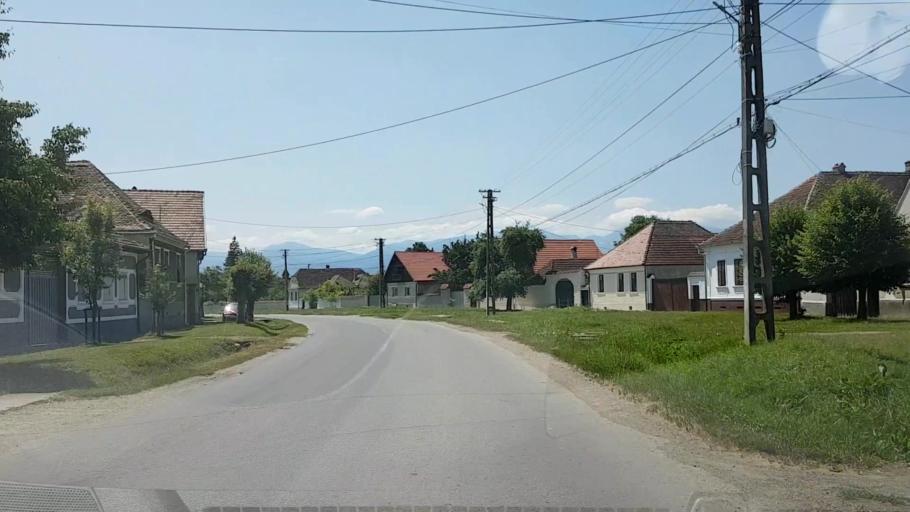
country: RO
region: Brasov
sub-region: Comuna Voila
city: Voila
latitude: 45.8390
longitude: 24.8326
